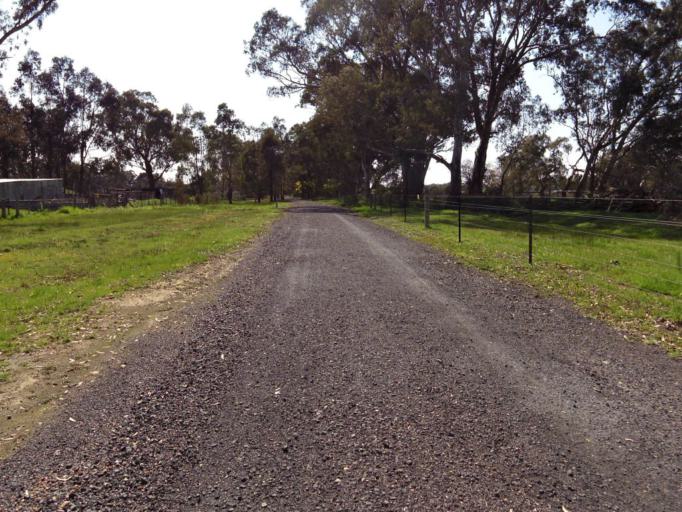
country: AU
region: Victoria
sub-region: Murrindindi
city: Alexandra
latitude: -37.1094
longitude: 145.6128
